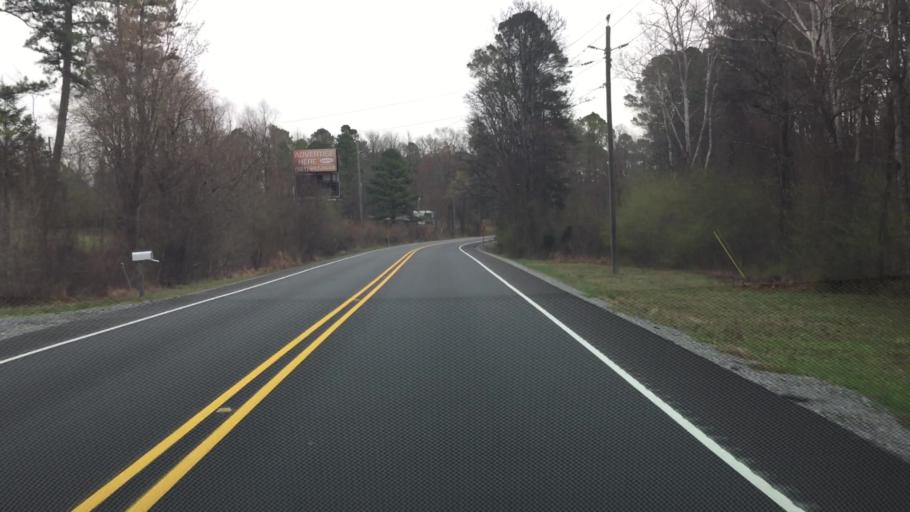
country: US
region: Arkansas
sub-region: Saline County
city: Haskell
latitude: 34.6143
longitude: -92.7913
